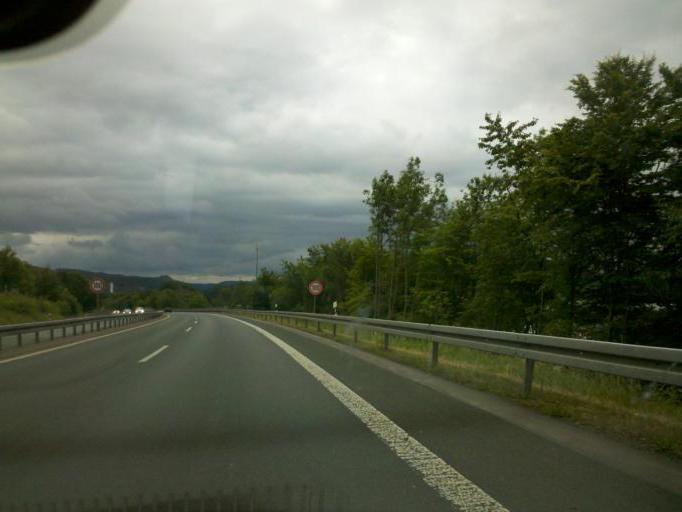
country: DE
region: North Rhine-Westphalia
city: Kreuztal
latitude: 50.9417
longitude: 8.0056
